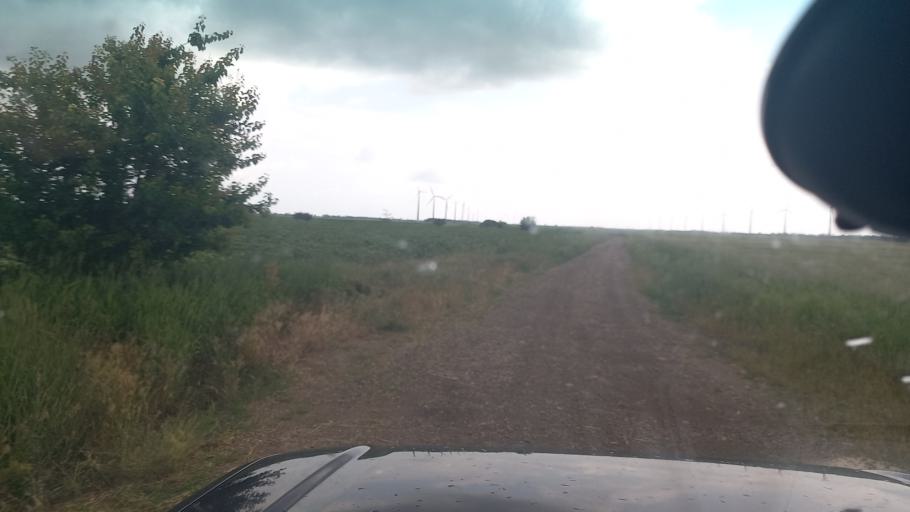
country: RU
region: Adygeya
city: Shovgenovskiy
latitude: 44.9956
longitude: 40.1223
